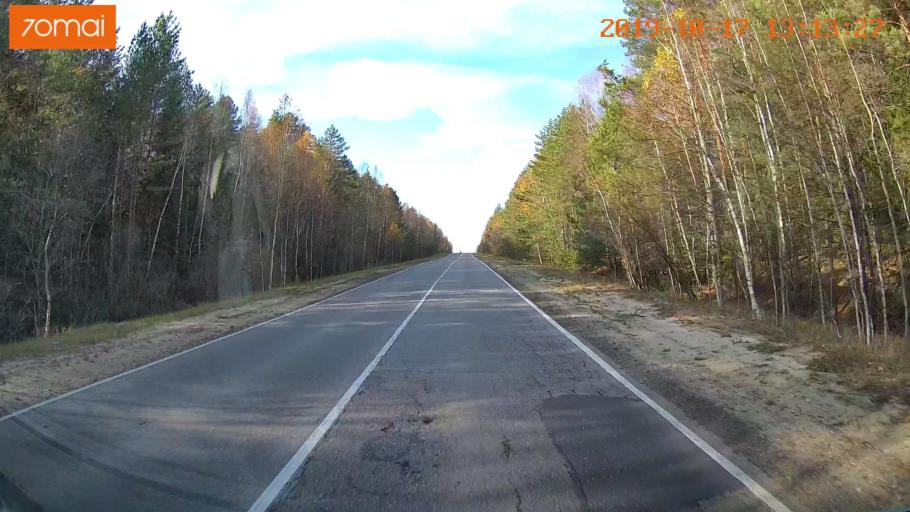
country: RU
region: Rjazan
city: Gus'-Zheleznyy
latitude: 55.0451
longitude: 41.1908
